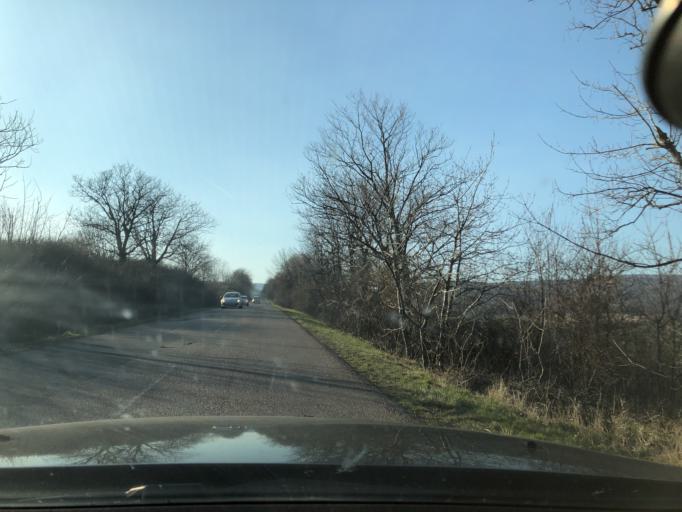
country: HU
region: Nograd
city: Paszto
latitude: 47.9102
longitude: 19.6572
